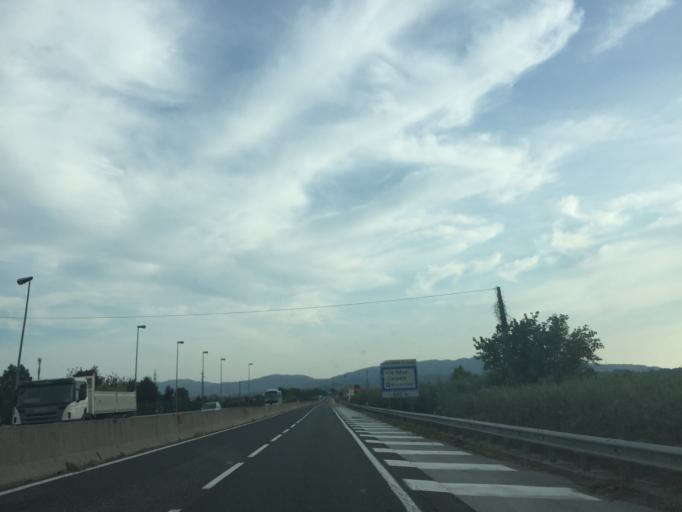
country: IT
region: Tuscany
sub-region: Provincia di Pistoia
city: Pistoia
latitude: 43.9501
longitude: 10.8965
